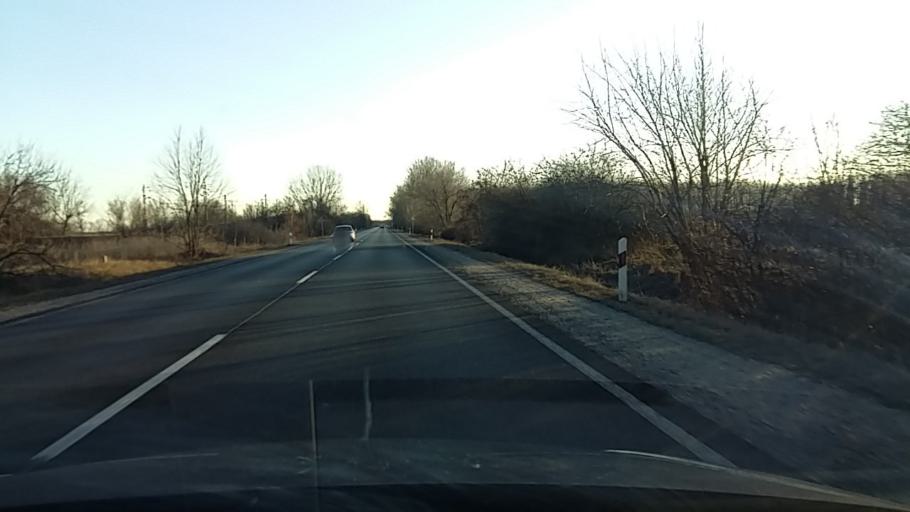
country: HU
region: Szabolcs-Szatmar-Bereg
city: Ujfeherto
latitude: 47.8451
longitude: 21.7044
